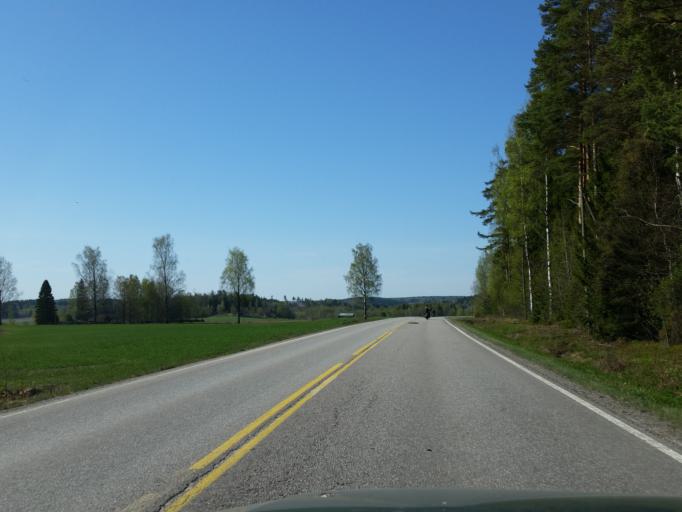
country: FI
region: Uusimaa
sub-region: Helsinki
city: Siuntio
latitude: 60.1874
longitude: 24.2443
